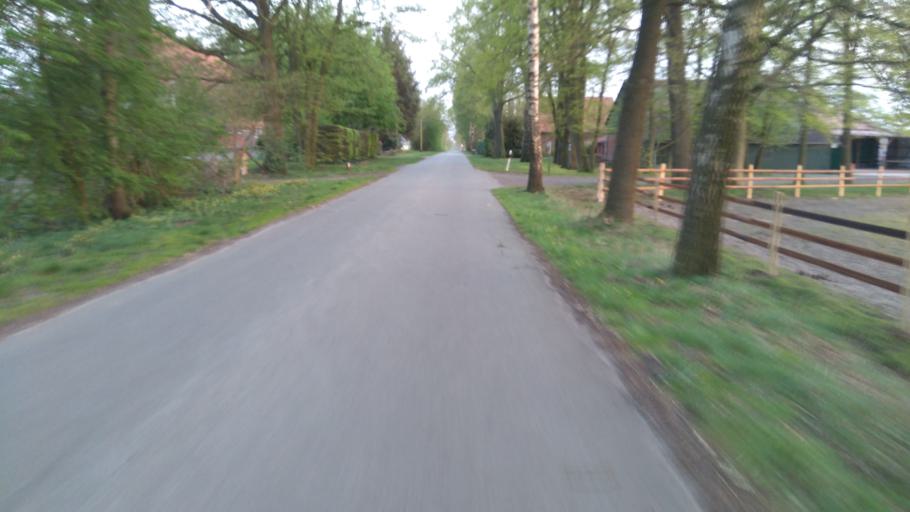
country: DE
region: Lower Saxony
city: Bargstedt
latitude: 53.4820
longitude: 9.4778
